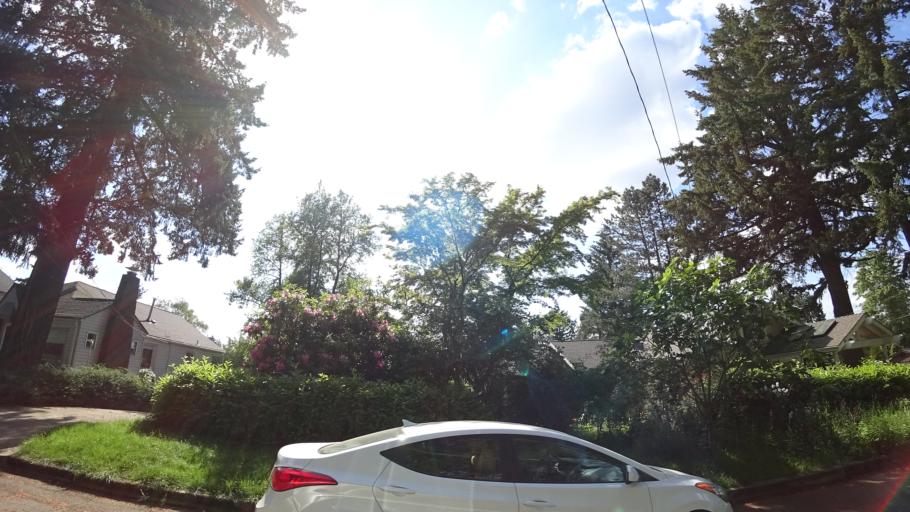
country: US
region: Oregon
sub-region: Washington County
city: Garden Home-Whitford
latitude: 45.4651
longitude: -122.7205
